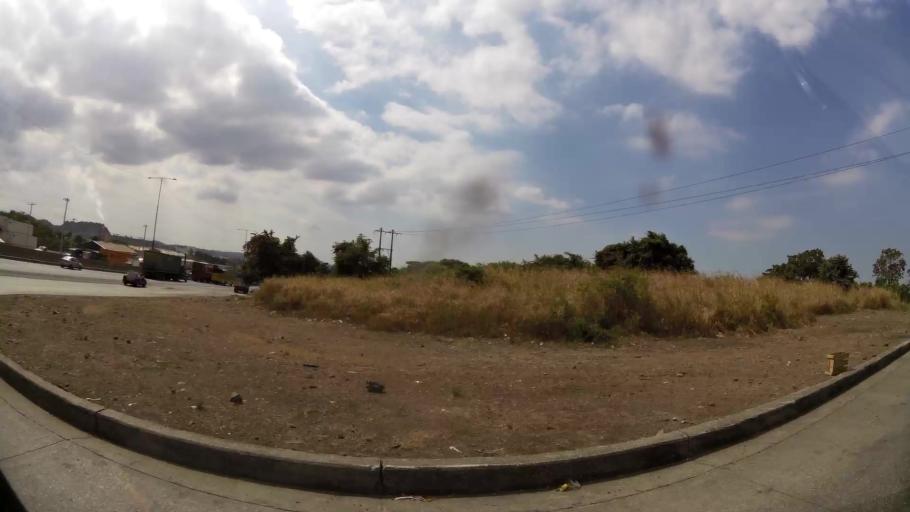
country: EC
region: Guayas
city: Santa Lucia
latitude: -2.0934
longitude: -79.9476
